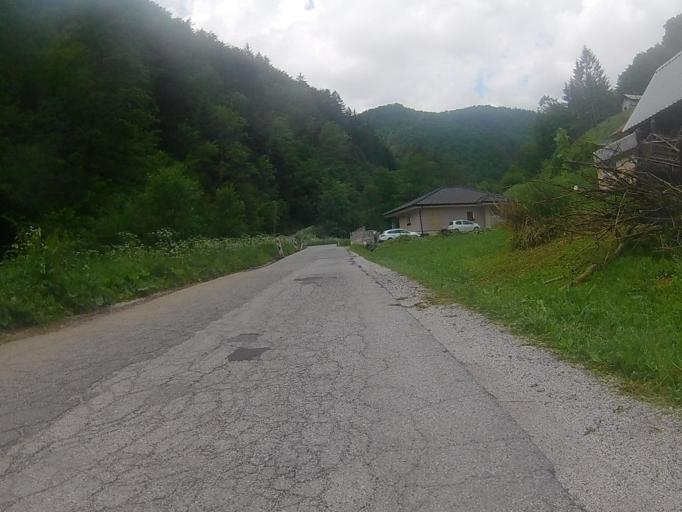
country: SI
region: Maribor
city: Bresternica
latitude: 46.5893
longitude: 15.5592
